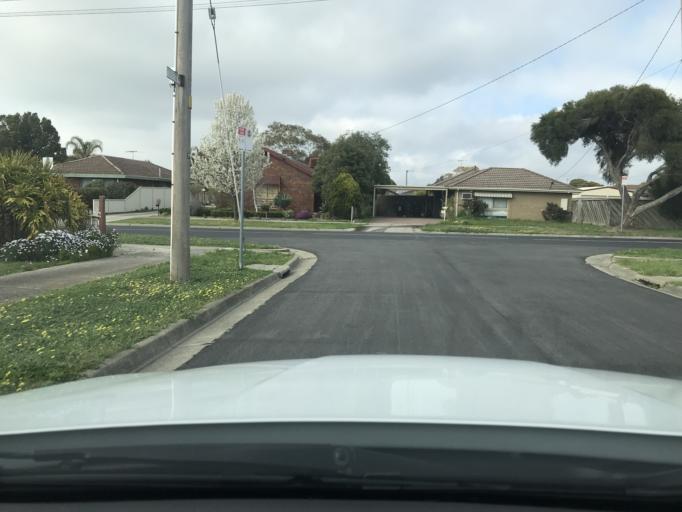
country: AU
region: Victoria
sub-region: Hume
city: Craigieburn
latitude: -37.6015
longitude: 144.9407
